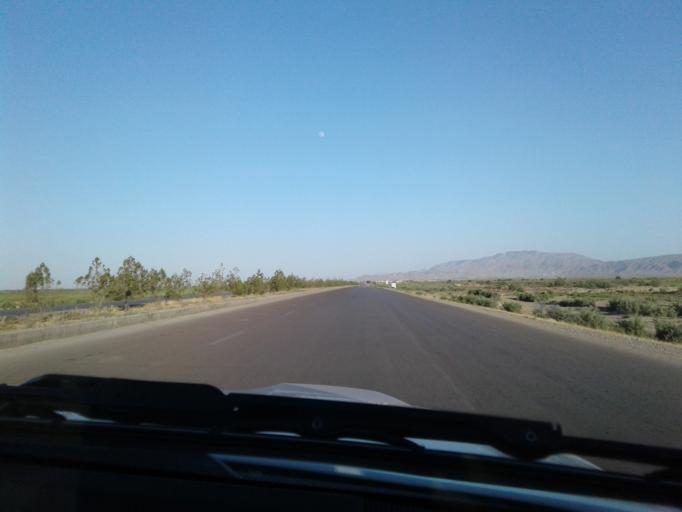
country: TM
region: Ahal
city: Baharly
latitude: 38.3573
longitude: 57.5377
